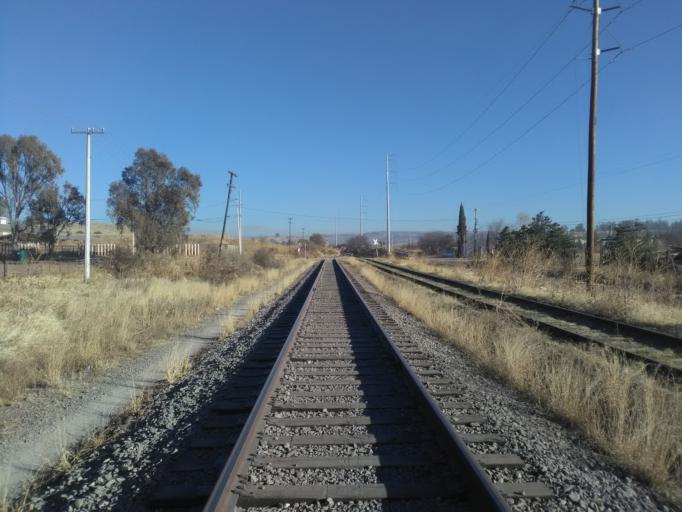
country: MX
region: Durango
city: Victoria de Durango
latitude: 24.0614
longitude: -104.6538
